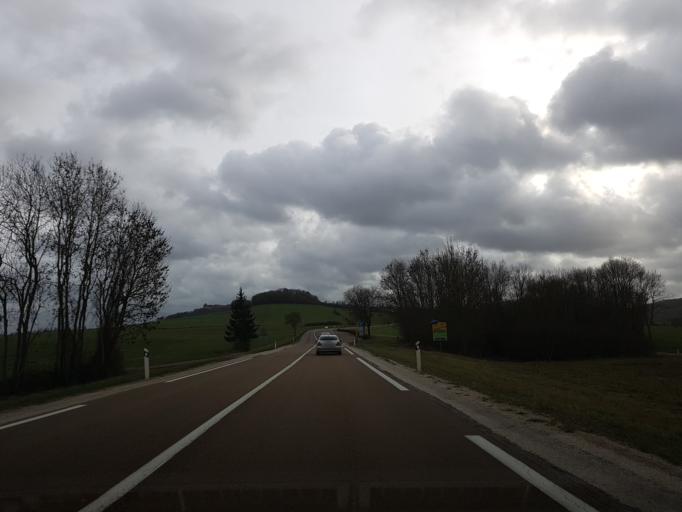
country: FR
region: Champagne-Ardenne
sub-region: Departement de la Haute-Marne
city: Langres
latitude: 47.8851
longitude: 5.3187
